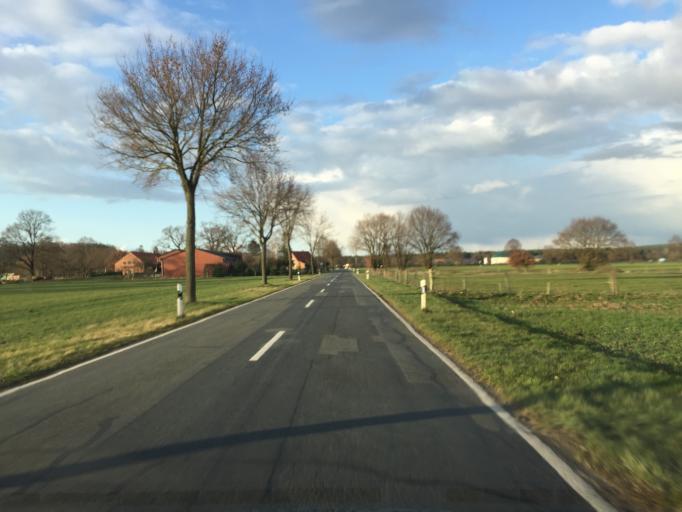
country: DE
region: Lower Saxony
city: Steyerberg
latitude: 52.5875
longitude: 8.9798
